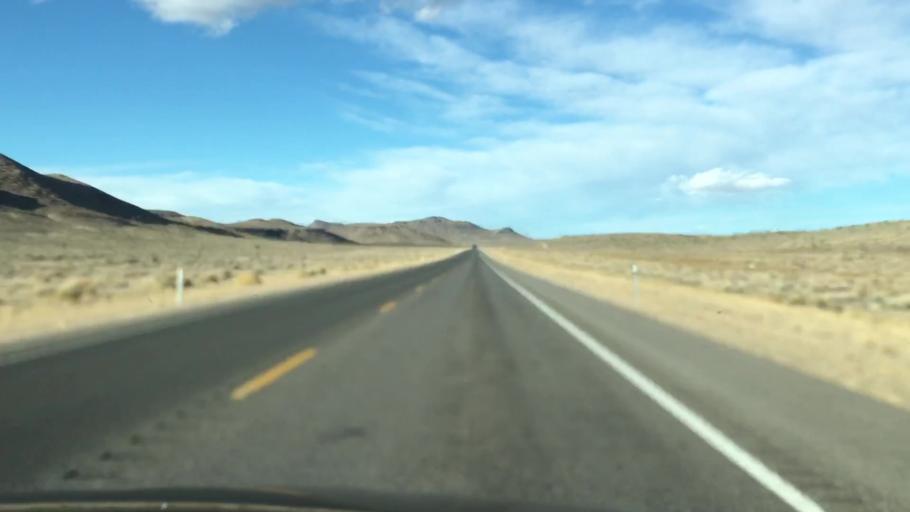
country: US
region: Nevada
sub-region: Esmeralda County
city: Goldfield
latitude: 37.6278
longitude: -117.2185
